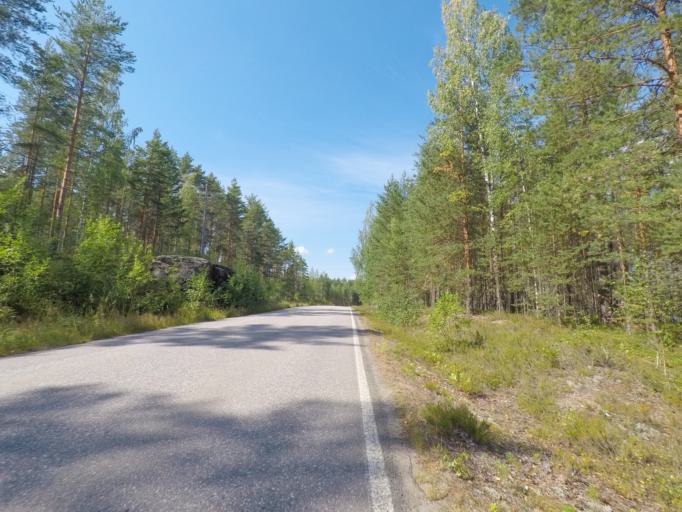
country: FI
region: Southern Savonia
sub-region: Mikkeli
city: Puumala
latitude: 61.4643
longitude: 28.1709
